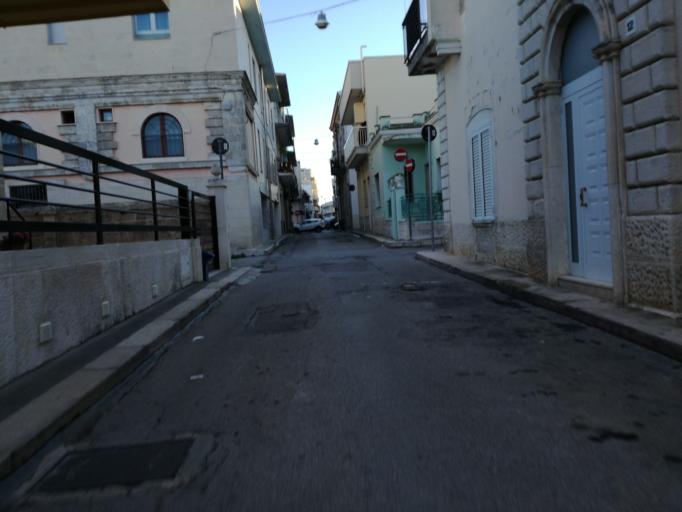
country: IT
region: Apulia
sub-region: Provincia di Bari
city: Adelfia
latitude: 41.0045
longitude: 16.8700
